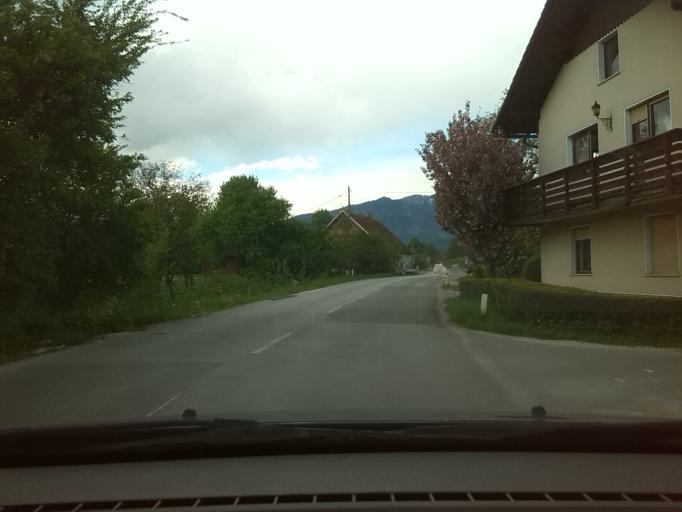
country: SI
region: Kamnik
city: Smarca
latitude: 46.1886
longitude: 14.6042
